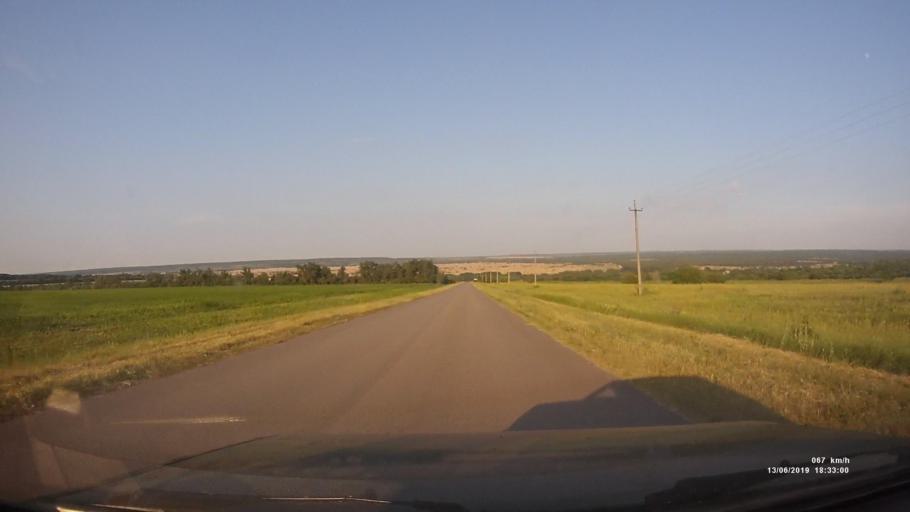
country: RU
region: Rostov
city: Kazanskaya
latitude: 49.8703
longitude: 41.3754
